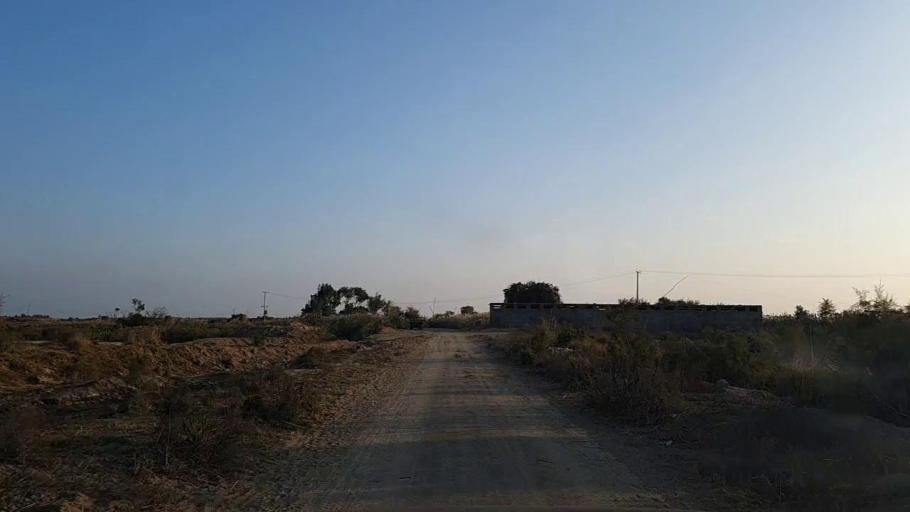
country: PK
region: Sindh
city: Sanghar
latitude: 26.2578
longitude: 68.9784
